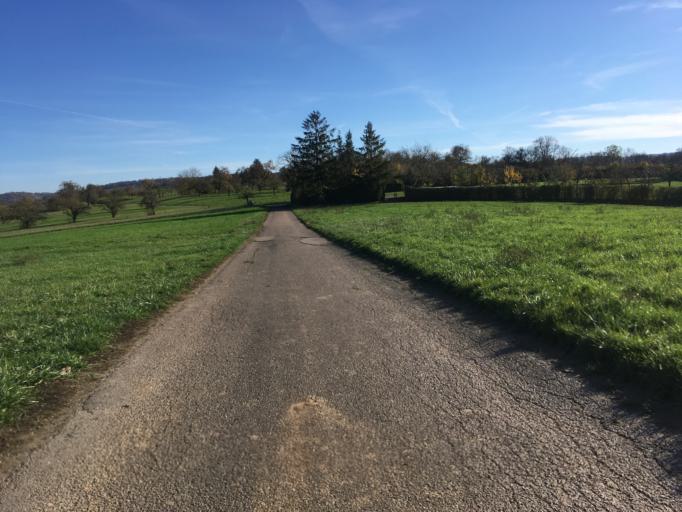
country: DE
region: Baden-Wuerttemberg
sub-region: Karlsruhe Region
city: Oberderdingen
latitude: 49.0739
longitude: 8.8040
